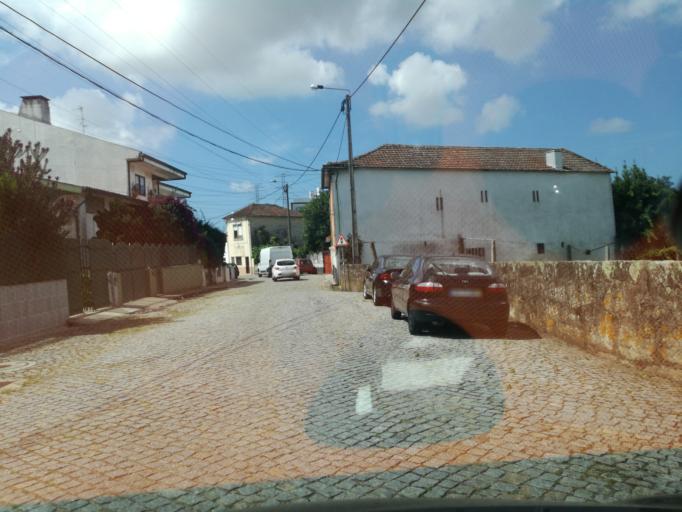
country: PT
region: Porto
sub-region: Maia
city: Nogueira
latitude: 41.2351
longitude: -8.5945
